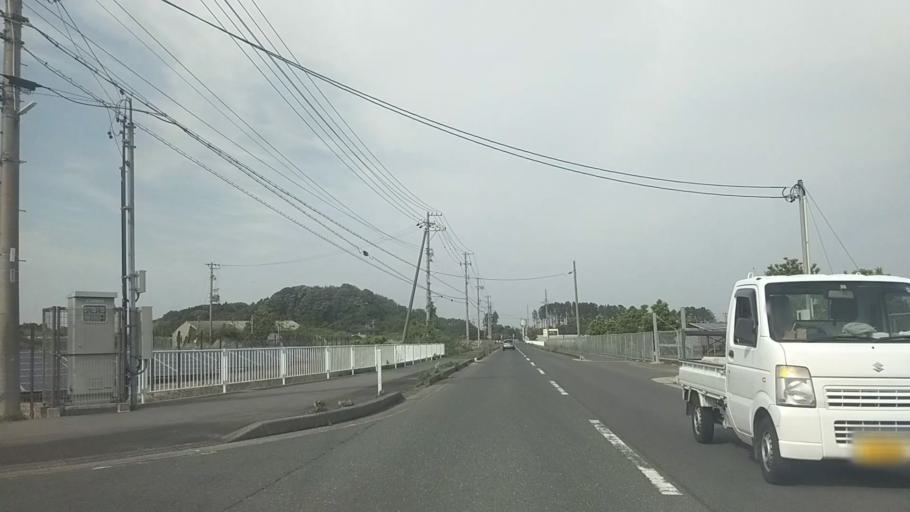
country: JP
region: Shizuoka
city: Kosai-shi
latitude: 34.7238
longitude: 137.6009
